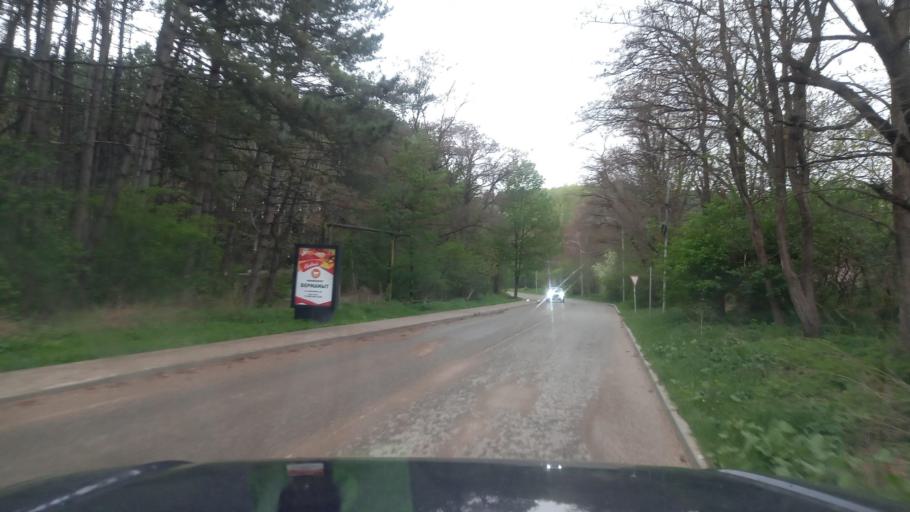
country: RU
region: Stavropol'skiy
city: Kislovodsk
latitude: 43.8884
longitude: 42.6996
